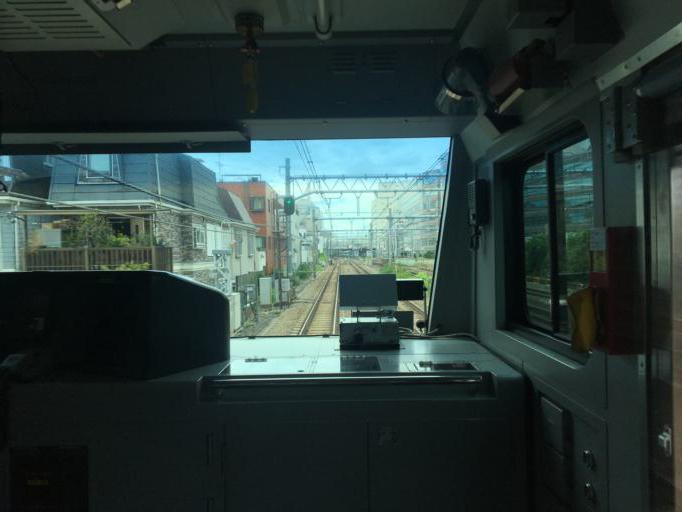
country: JP
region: Kanagawa
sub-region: Kawasaki-shi
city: Kawasaki
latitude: 35.5662
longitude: 139.7177
